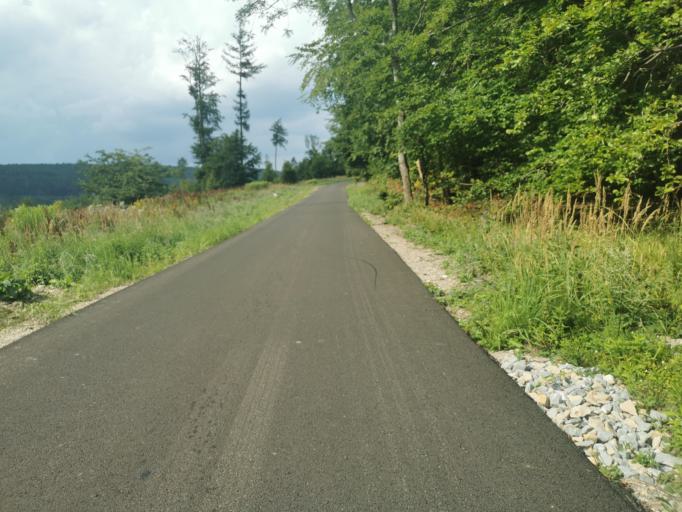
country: SK
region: Trenciansky
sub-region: Okres Myjava
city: Myjava
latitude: 48.8219
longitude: 17.6076
